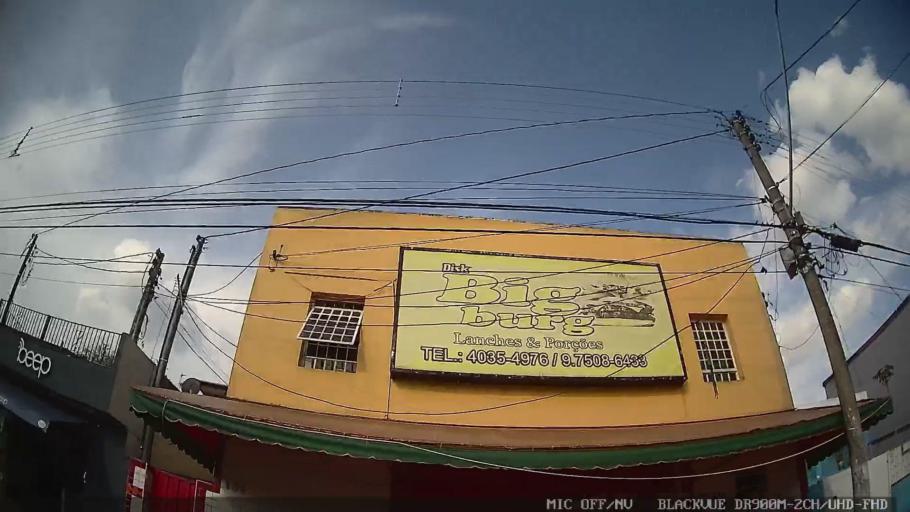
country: BR
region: Sao Paulo
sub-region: Braganca Paulista
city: Braganca Paulista
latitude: -22.9347
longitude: -46.5324
